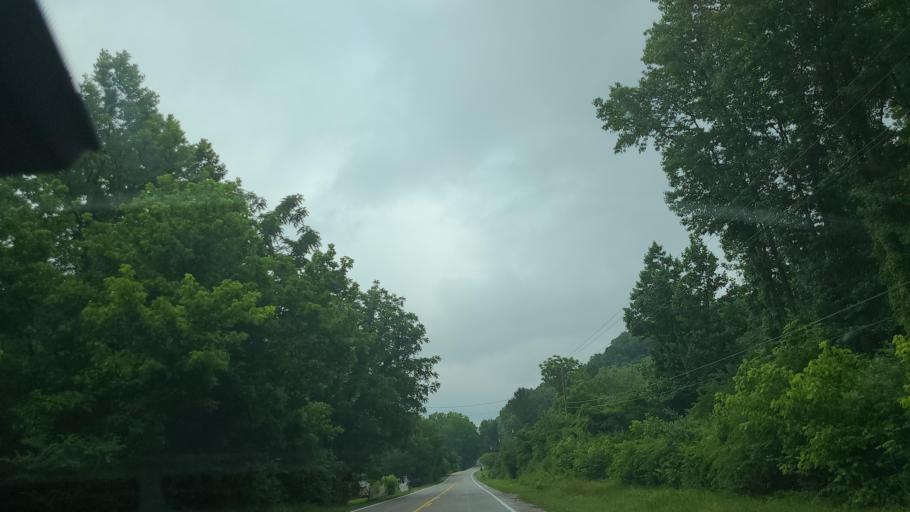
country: US
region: Tennessee
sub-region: Roane County
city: Oliver Springs
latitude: 36.0602
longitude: -84.3033
